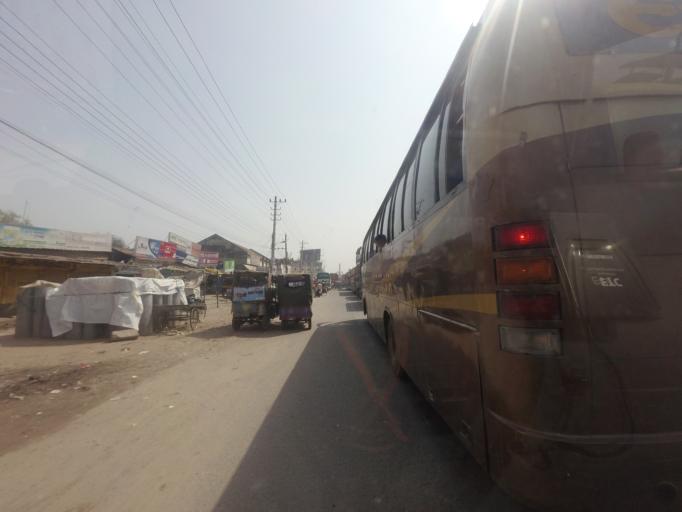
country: BD
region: Dhaka
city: Bhairab Bazar
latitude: 24.0553
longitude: 90.9806
